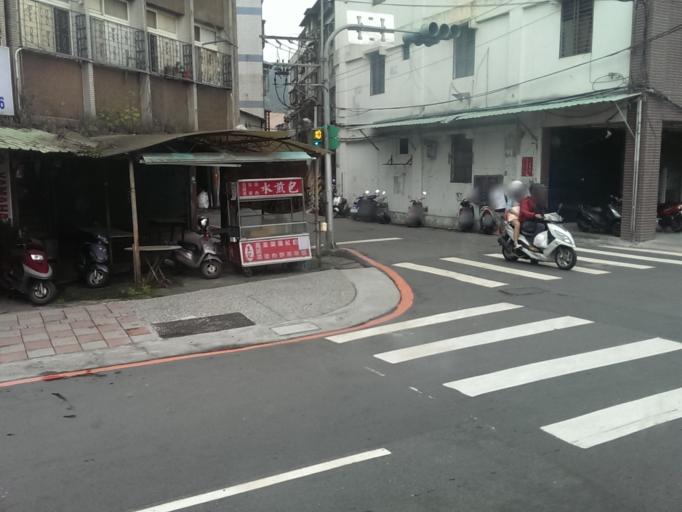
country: TW
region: Taipei
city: Taipei
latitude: 24.9772
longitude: 121.5492
